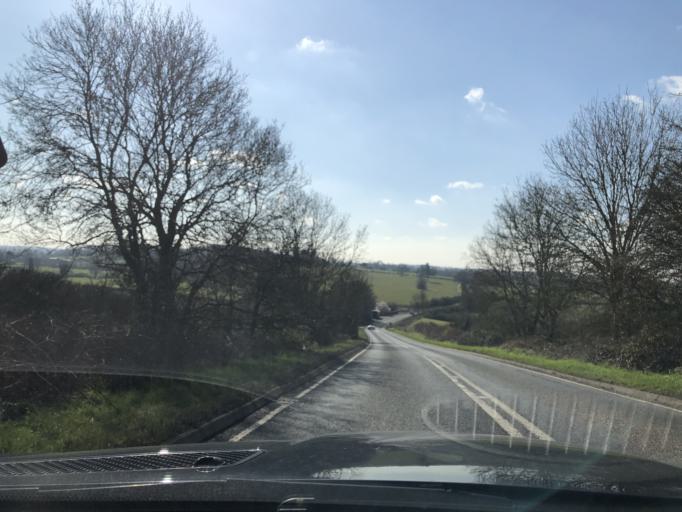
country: GB
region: England
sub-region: Warwickshire
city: Ryton on Dunsmore
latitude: 52.3285
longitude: -1.4163
